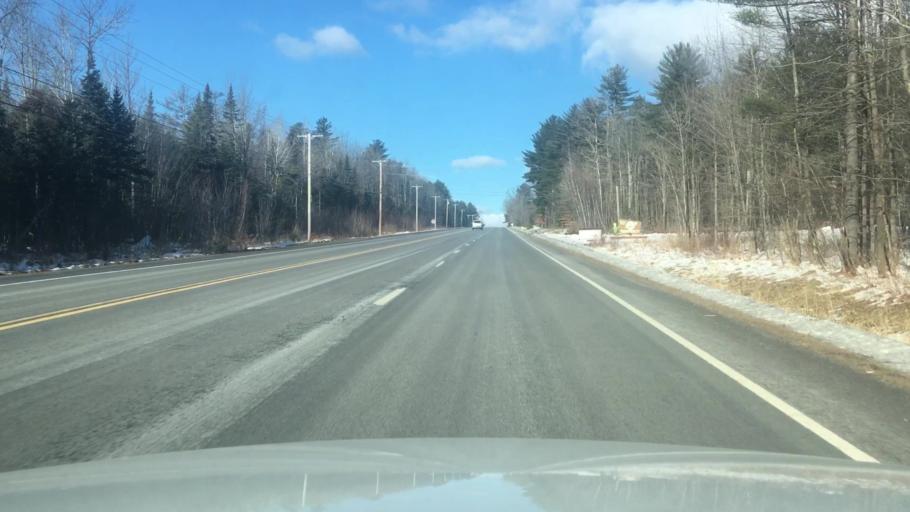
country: US
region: Maine
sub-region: Somerset County
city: Skowhegan
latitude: 44.7977
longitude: -69.7496
